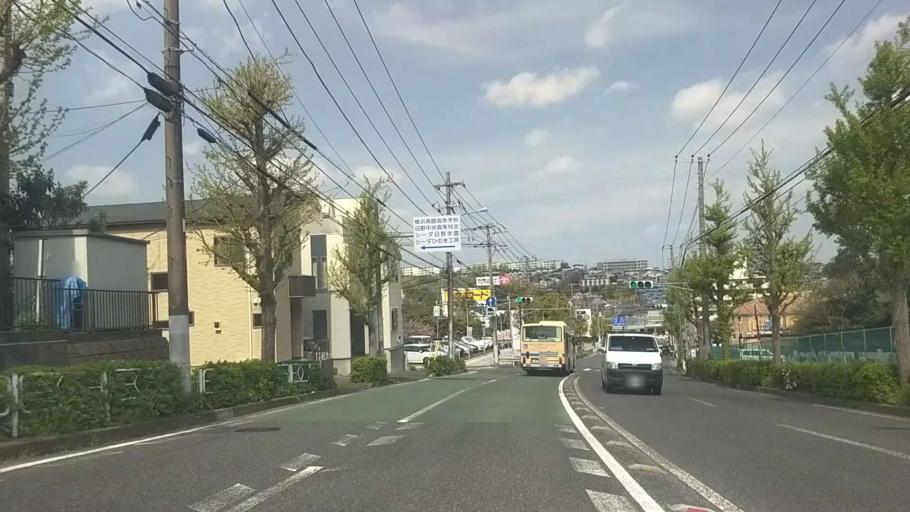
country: JP
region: Kanagawa
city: Yokohama
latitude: 35.3884
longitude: 139.5847
